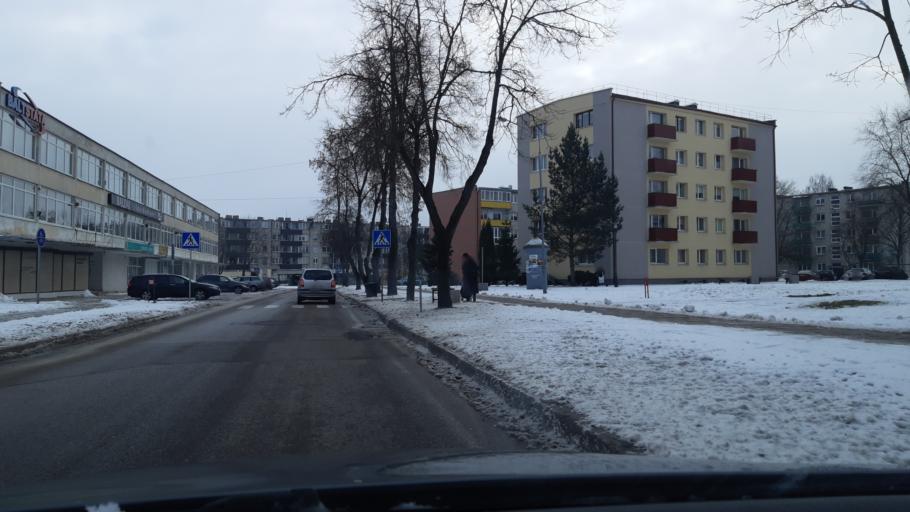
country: LT
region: Kauno apskritis
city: Kedainiai
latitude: 55.2911
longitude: 23.9823
